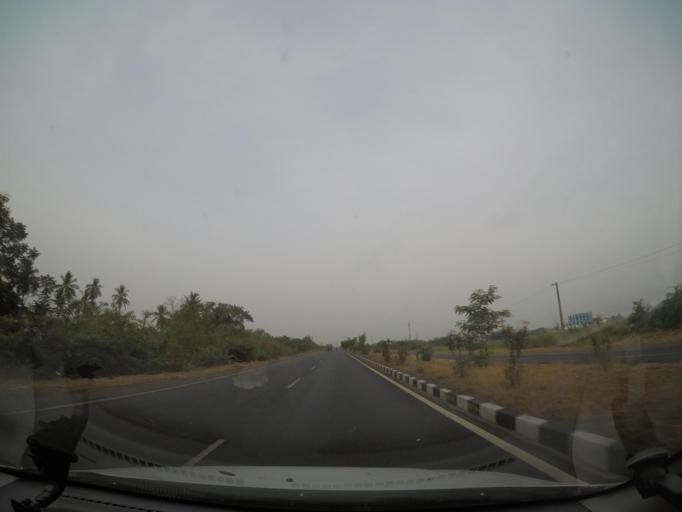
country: IN
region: Andhra Pradesh
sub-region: Krishna
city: Gannavaram
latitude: 16.6223
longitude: 80.9337
